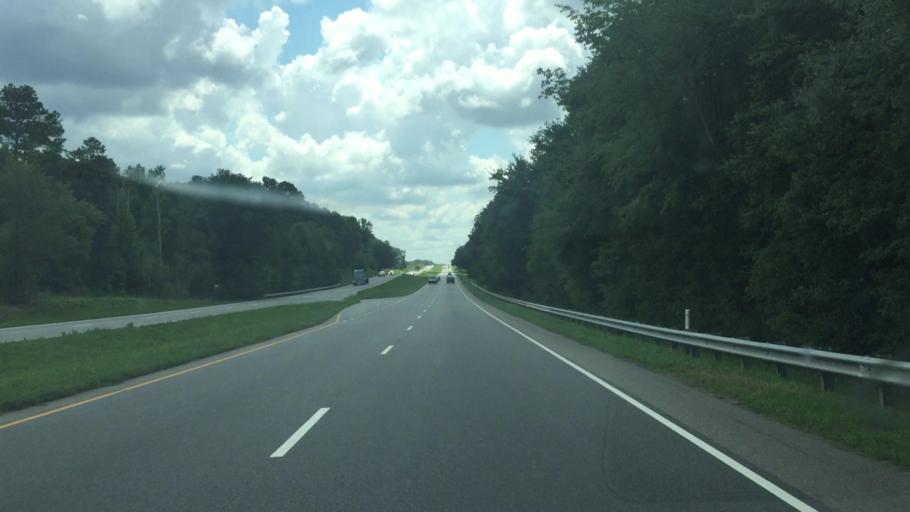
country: US
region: North Carolina
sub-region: Richmond County
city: Hamlet
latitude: 34.8579
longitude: -79.6283
